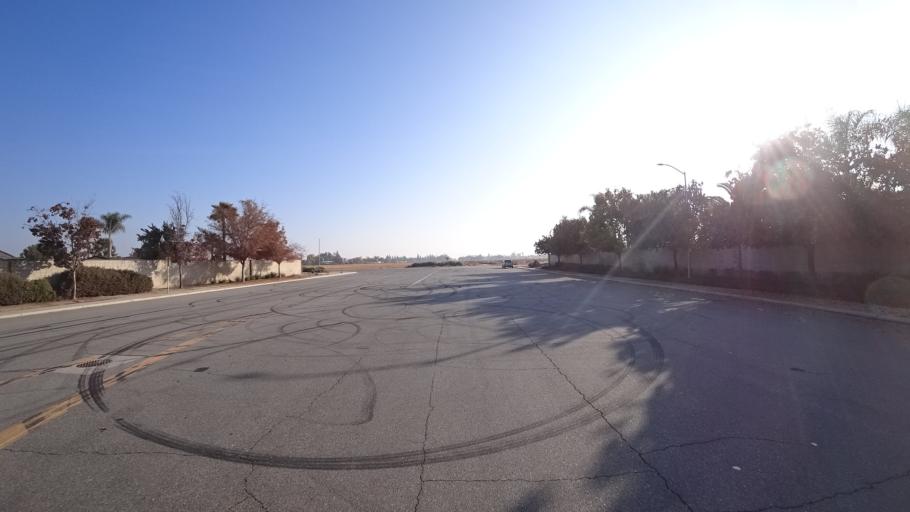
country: US
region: California
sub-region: Kern County
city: Rosedale
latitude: 35.3689
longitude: -119.1732
